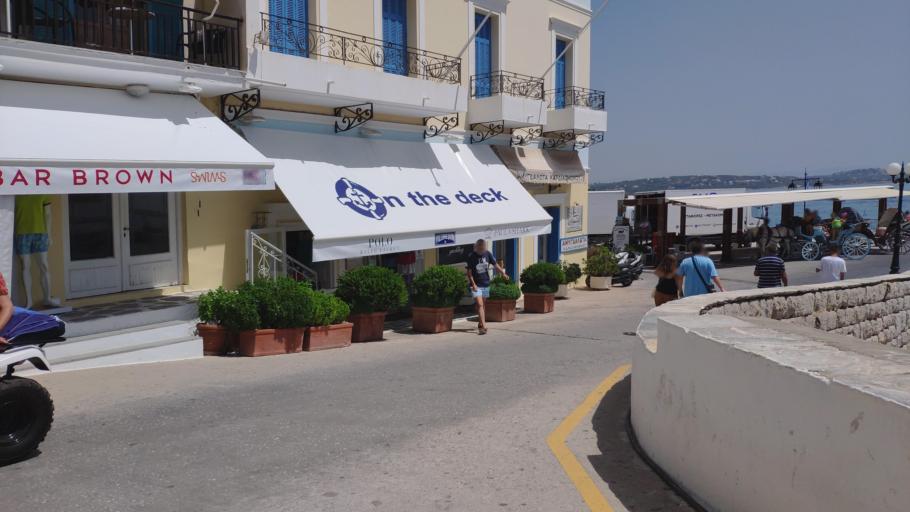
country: GR
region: Attica
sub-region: Nomos Piraios
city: Spetses
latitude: 37.2681
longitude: 23.1554
